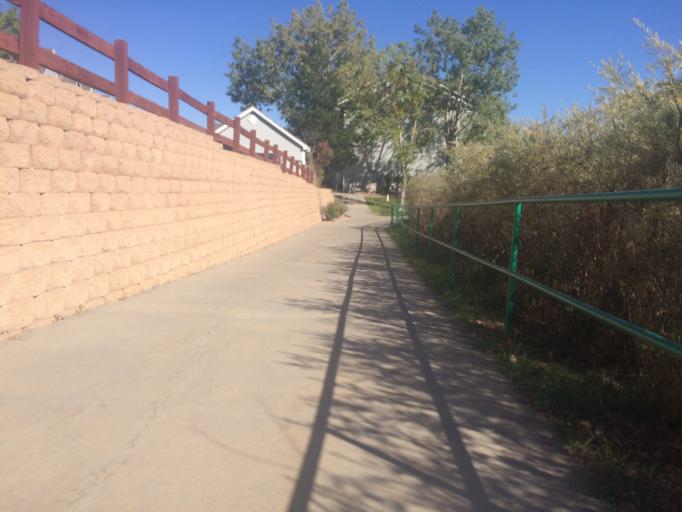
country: US
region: Colorado
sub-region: Broomfield County
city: Broomfield
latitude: 39.8790
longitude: -105.0782
